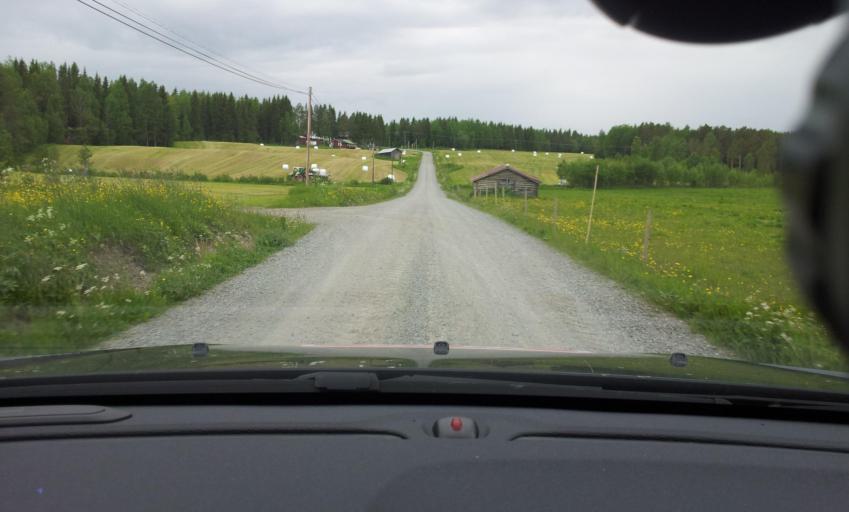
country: SE
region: Jaemtland
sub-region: OEstersunds Kommun
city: Brunflo
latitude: 62.9735
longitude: 14.6793
